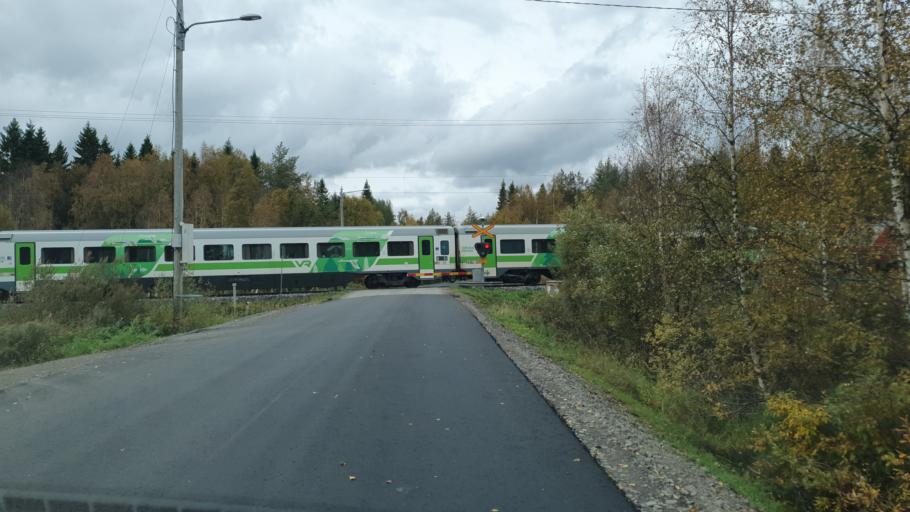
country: FI
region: Lapland
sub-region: Rovaniemi
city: Rovaniemi
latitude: 66.4204
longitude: 25.4086
